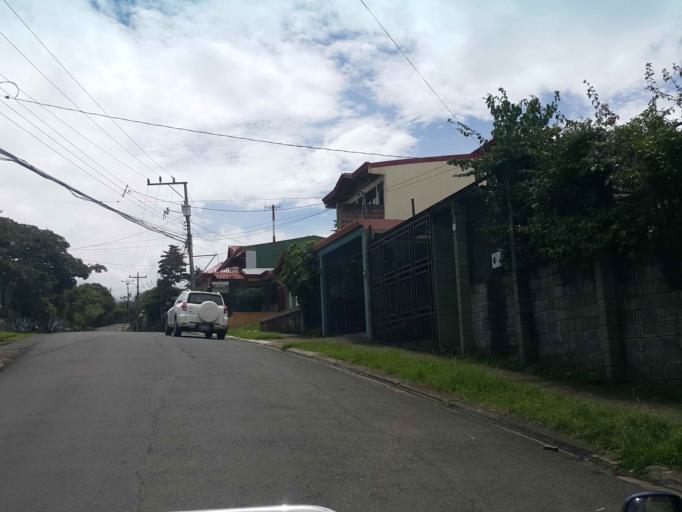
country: CR
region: Heredia
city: Heredia
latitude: 10.0165
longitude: -84.1149
